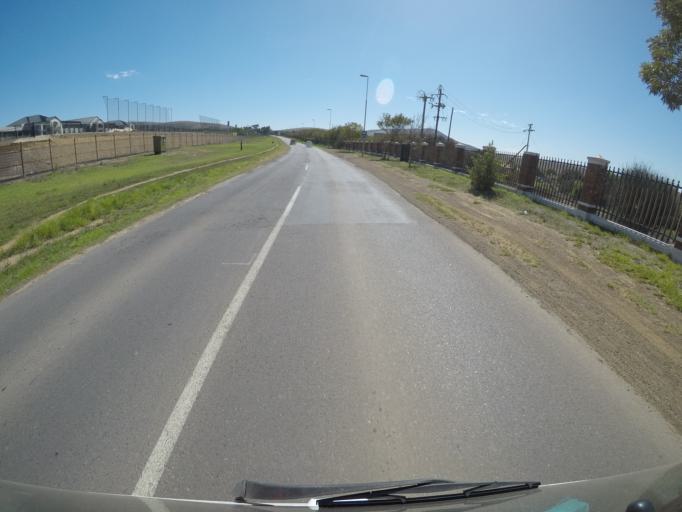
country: ZA
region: Western Cape
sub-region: City of Cape Town
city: Kraaifontein
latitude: -33.8156
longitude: 18.6333
